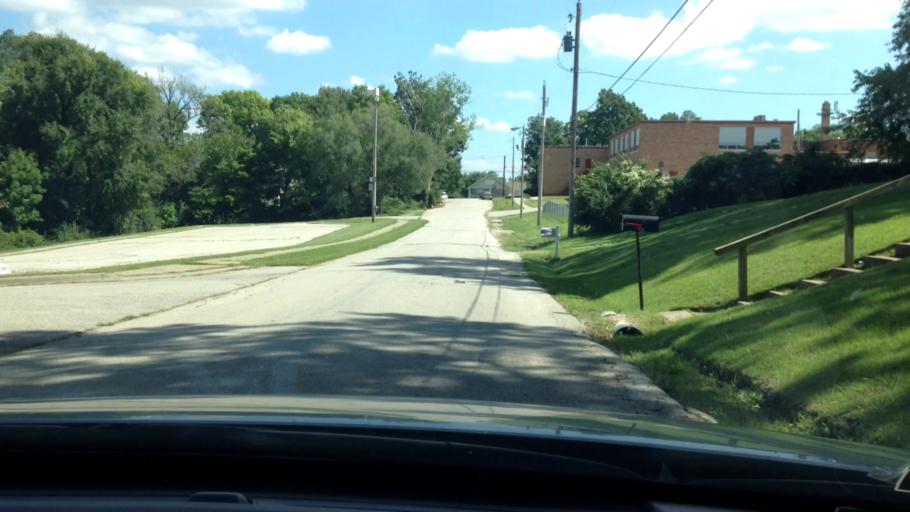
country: US
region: Kansas
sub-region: Leavenworth County
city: Leavenworth
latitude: 39.3122
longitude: -94.9319
